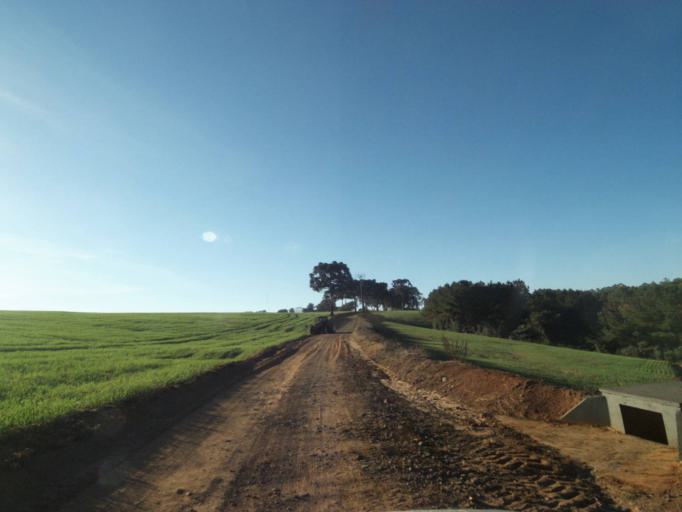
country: BR
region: Parana
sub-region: Telemaco Borba
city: Telemaco Borba
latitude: -24.4755
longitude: -50.5874
